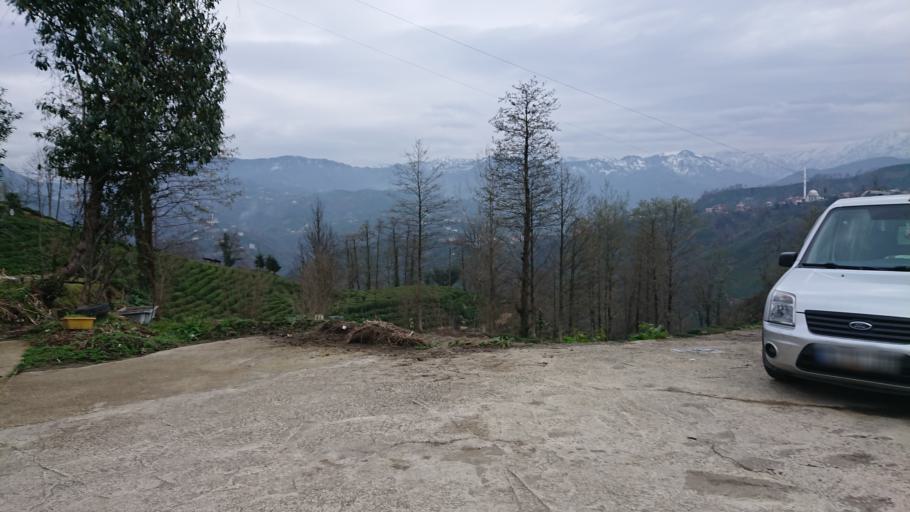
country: TR
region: Rize
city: Rize
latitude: 40.9704
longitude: 40.5180
